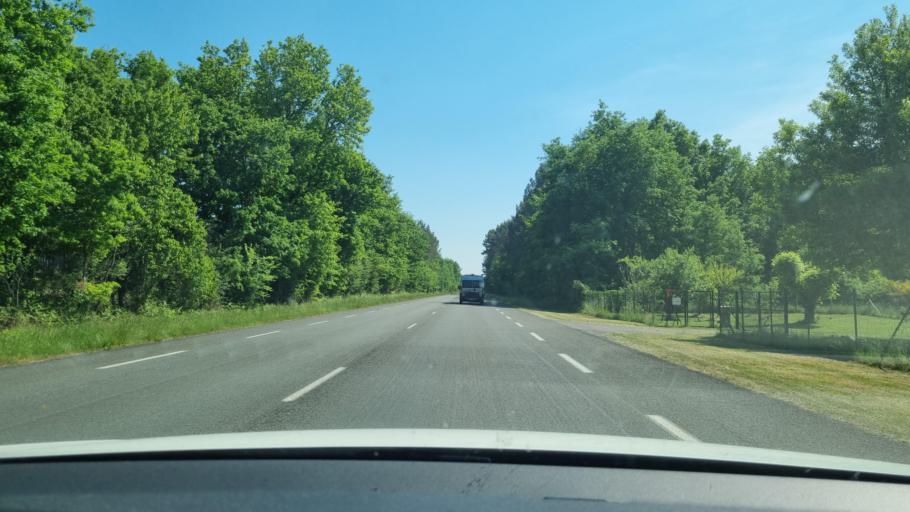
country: FR
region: Aquitaine
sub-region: Departement de la Gironde
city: Prechac
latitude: 44.2549
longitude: -0.2612
